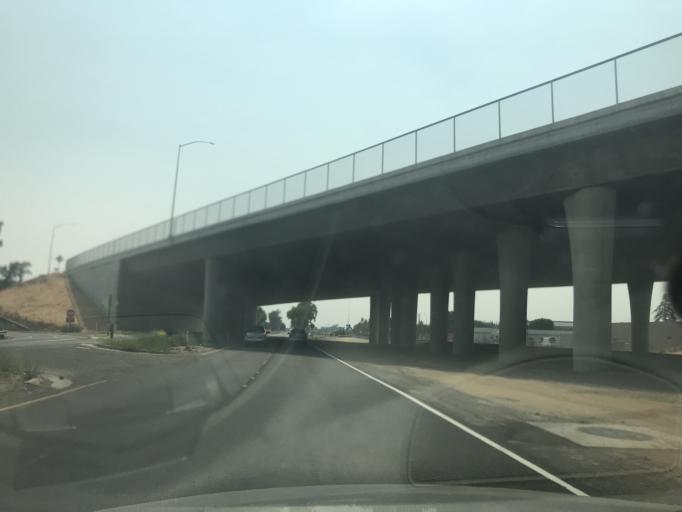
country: US
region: California
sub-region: Merced County
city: Merced
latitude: 37.2961
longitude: -120.4735
